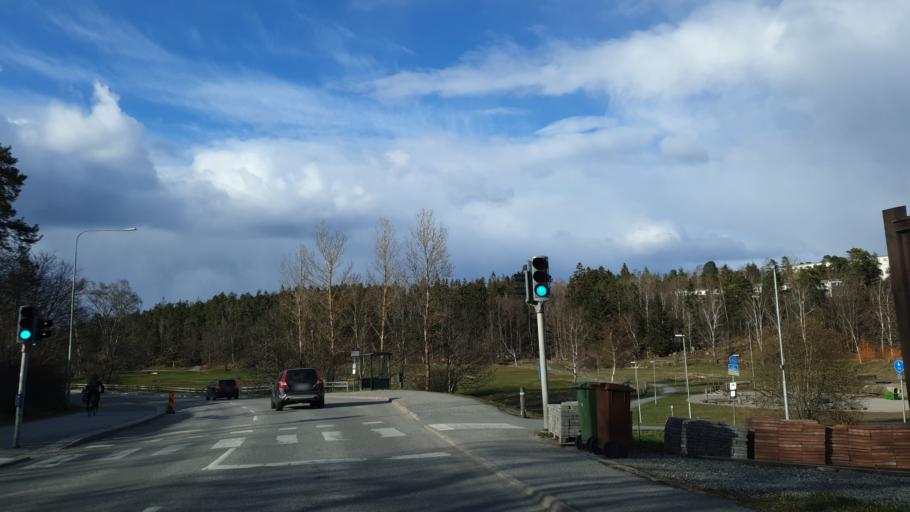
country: SE
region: Stockholm
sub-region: Lidingo
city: Lidingoe
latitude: 59.3725
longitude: 18.1330
